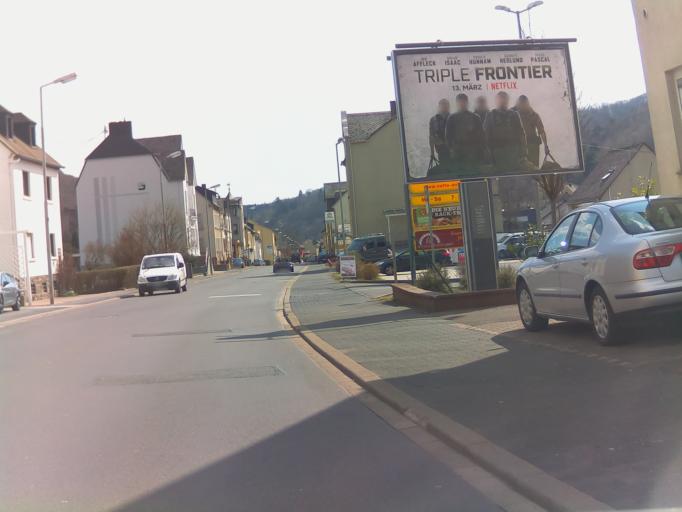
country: DE
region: Rheinland-Pfalz
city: Veitsrodt
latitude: 49.7411
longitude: 7.2796
